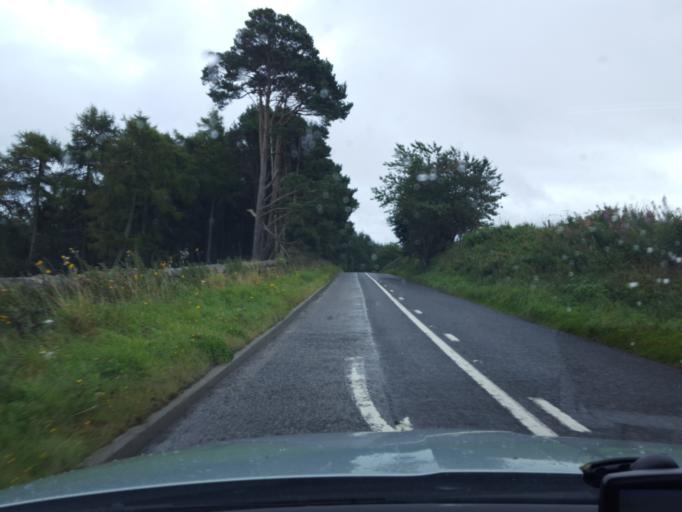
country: GB
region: Scotland
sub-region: Aberdeenshire
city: Stonehaven
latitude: 56.9815
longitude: -2.2492
